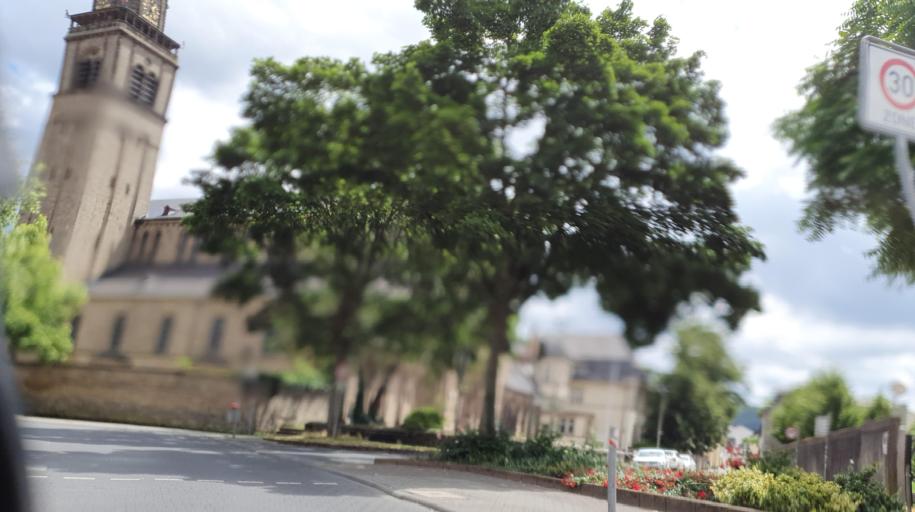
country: DE
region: Rheinland-Pfalz
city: Trier
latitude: 49.7645
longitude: 6.6429
